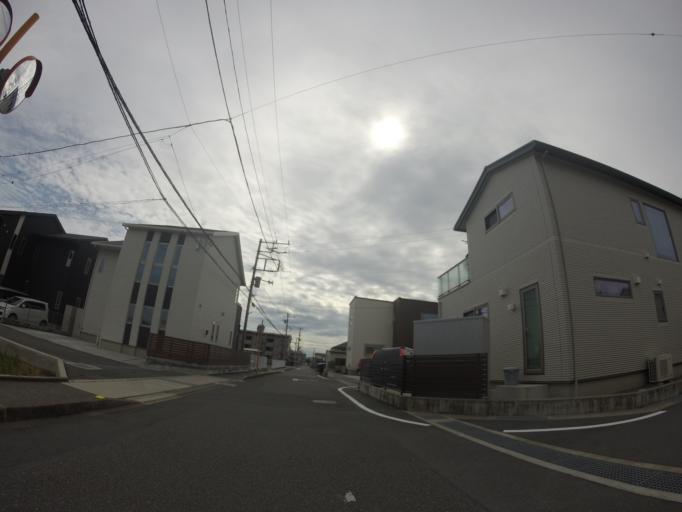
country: JP
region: Shizuoka
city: Fuji
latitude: 35.1381
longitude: 138.6435
